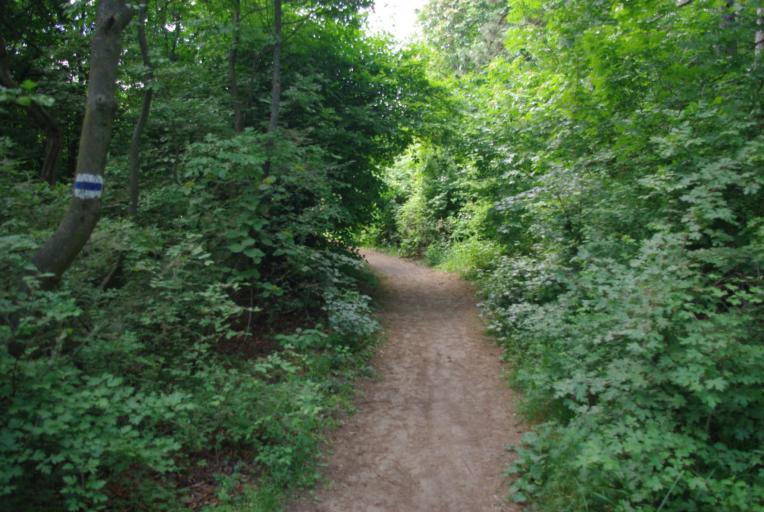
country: HU
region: Pest
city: Pilisszentivan
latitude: 47.5886
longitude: 18.8890
